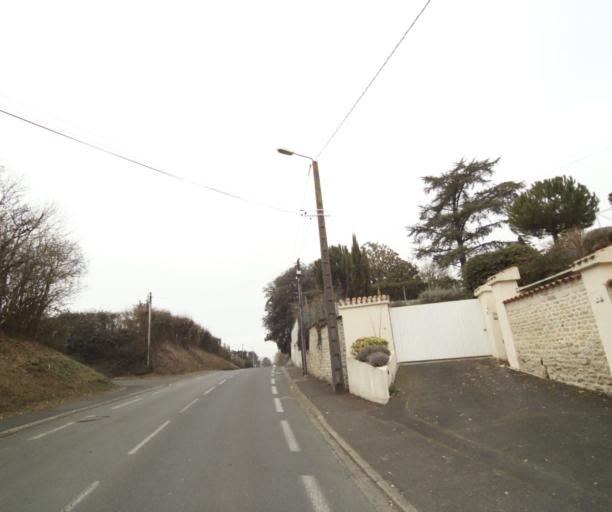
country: FR
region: Poitou-Charentes
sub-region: Departement des Deux-Sevres
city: Bessines
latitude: 46.3194
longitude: -0.5087
